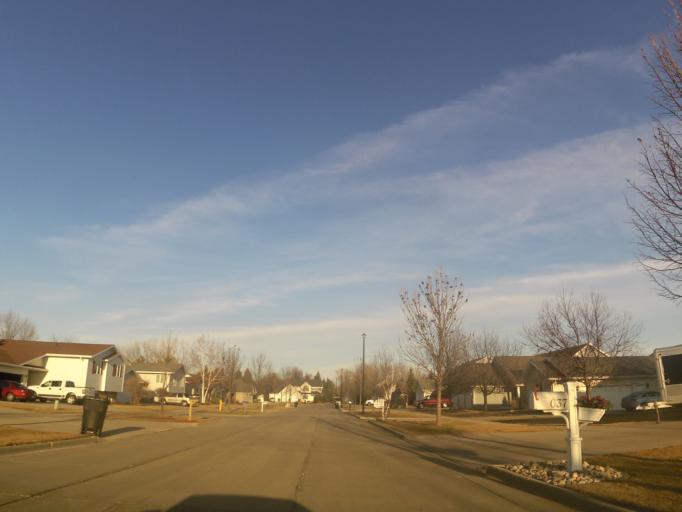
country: US
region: North Dakota
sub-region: Grand Forks County
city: Grand Forks
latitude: 47.8714
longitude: -97.0351
